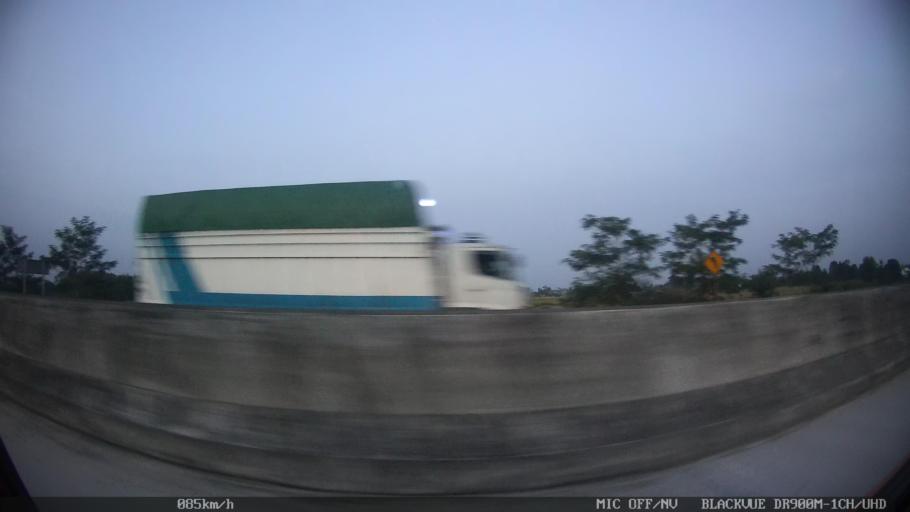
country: ID
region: Lampung
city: Sidorejo
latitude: -5.6293
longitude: 105.5664
